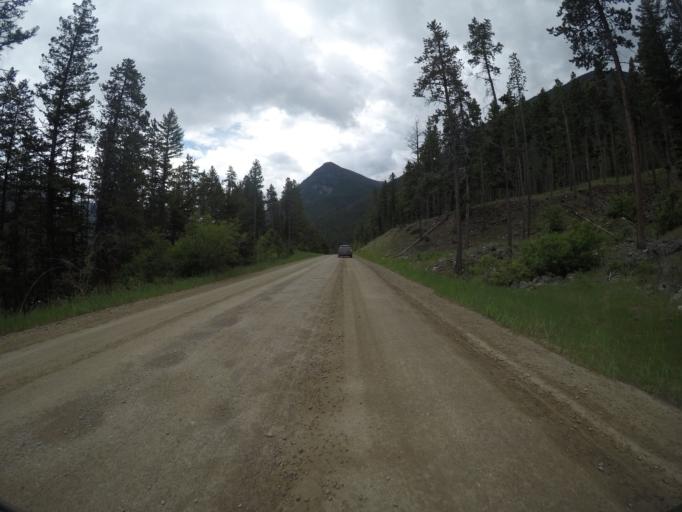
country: US
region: Montana
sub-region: Park County
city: Livingston
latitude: 45.4963
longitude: -110.2262
